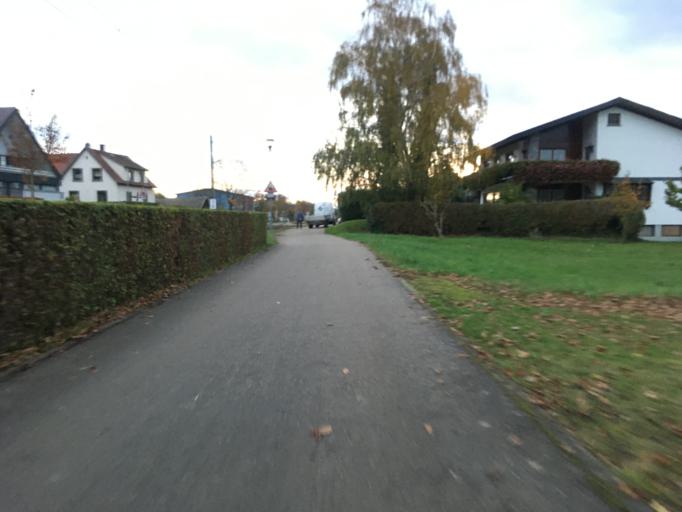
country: DE
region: Baden-Wuerttemberg
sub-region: Freiburg Region
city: Bahlingen
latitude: 48.1256
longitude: 7.7419
